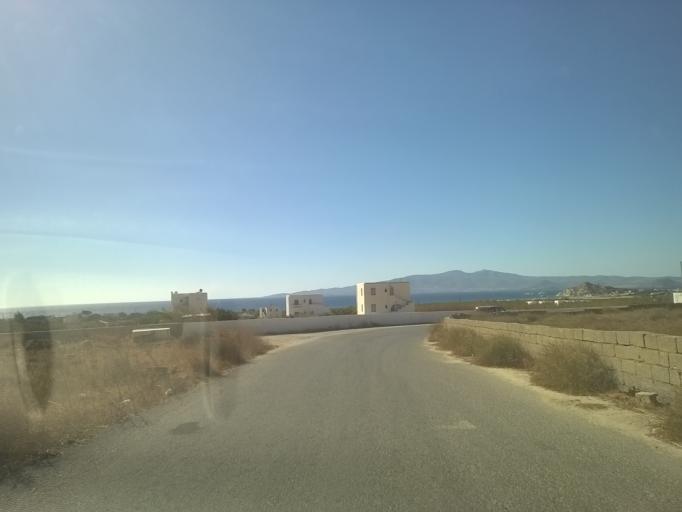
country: GR
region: South Aegean
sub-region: Nomos Kykladon
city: Naxos
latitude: 37.0150
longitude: 25.3942
